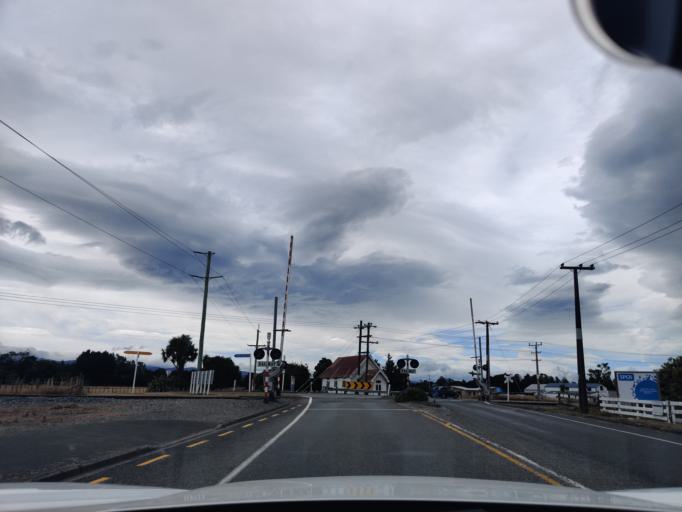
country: NZ
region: Wellington
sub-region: Masterton District
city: Masterton
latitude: -40.9584
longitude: 175.6140
